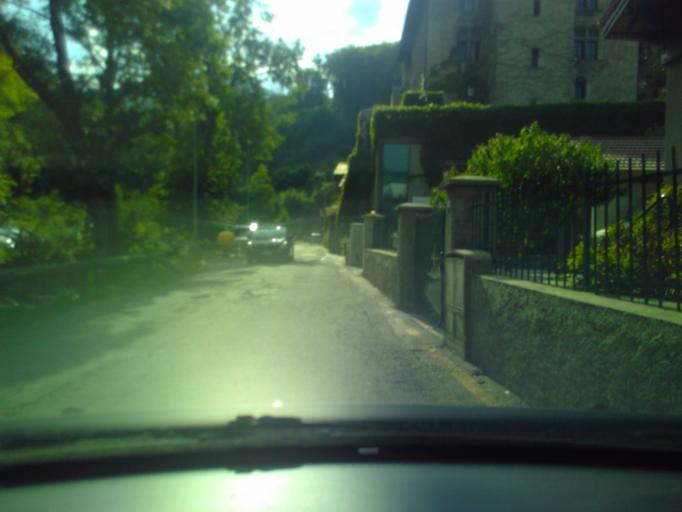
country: FR
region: Rhone-Alpes
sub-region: Departement de la Haute-Savoie
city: Sallanches
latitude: 45.9355
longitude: 6.6250
